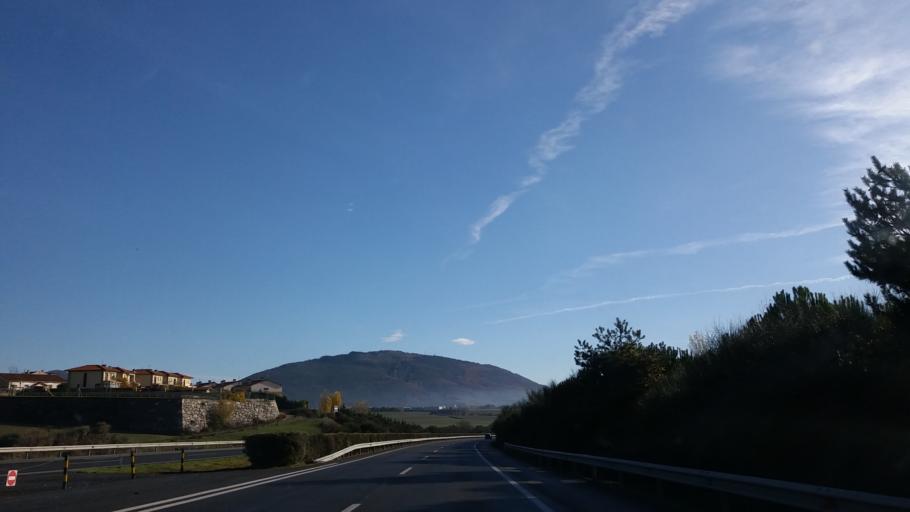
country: ES
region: Navarre
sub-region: Provincia de Navarra
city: Oltza
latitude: 42.8561
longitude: -1.7335
